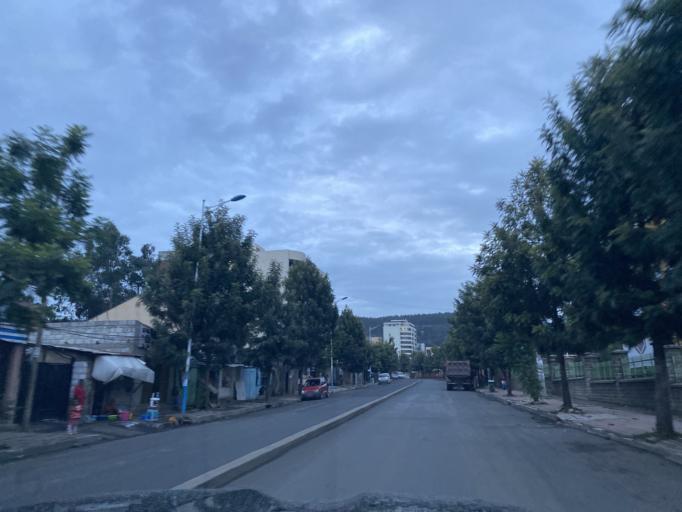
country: ET
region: Adis Abeba
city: Addis Ababa
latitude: 9.0159
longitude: 38.8116
